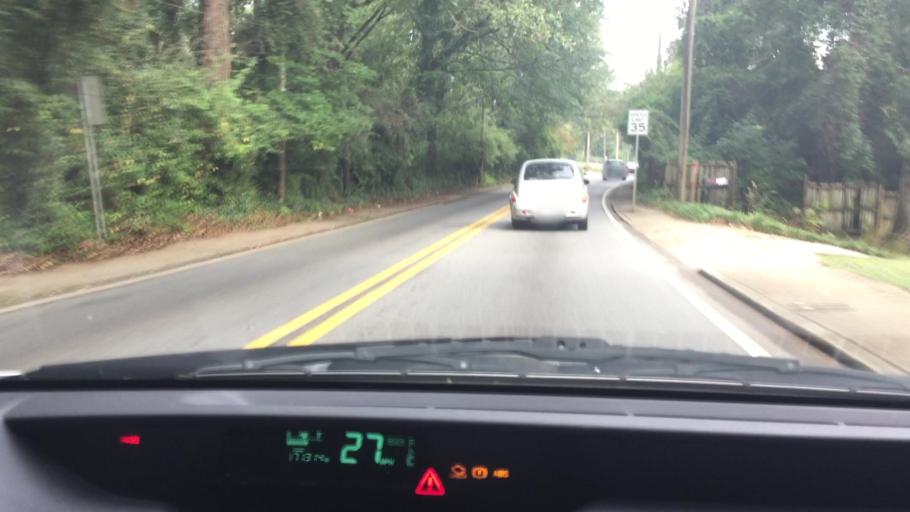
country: US
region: Georgia
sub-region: DeKalb County
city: Belvedere Park
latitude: 33.7491
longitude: -84.2923
